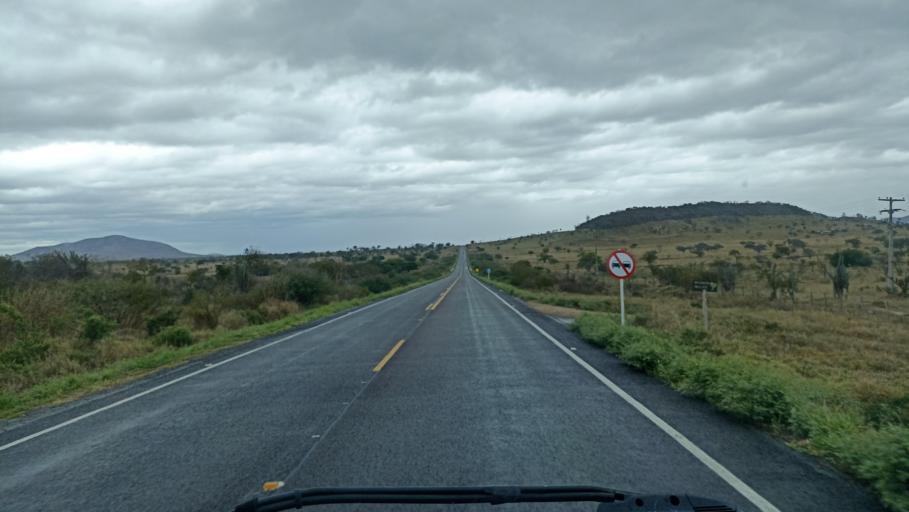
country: BR
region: Bahia
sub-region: Iacu
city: Iacu
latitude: -12.9616
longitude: -40.4801
